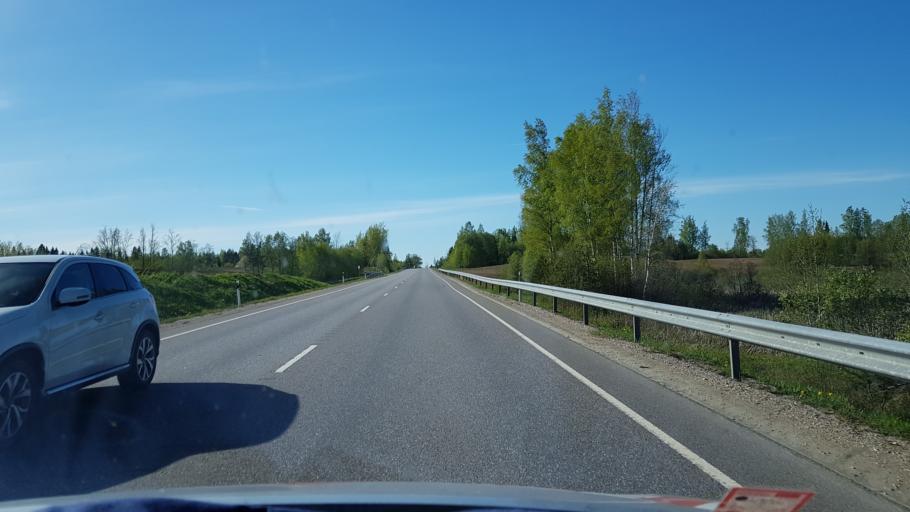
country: EE
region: Tartu
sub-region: UElenurme vald
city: Ulenurme
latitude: 58.1391
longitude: 26.7113
